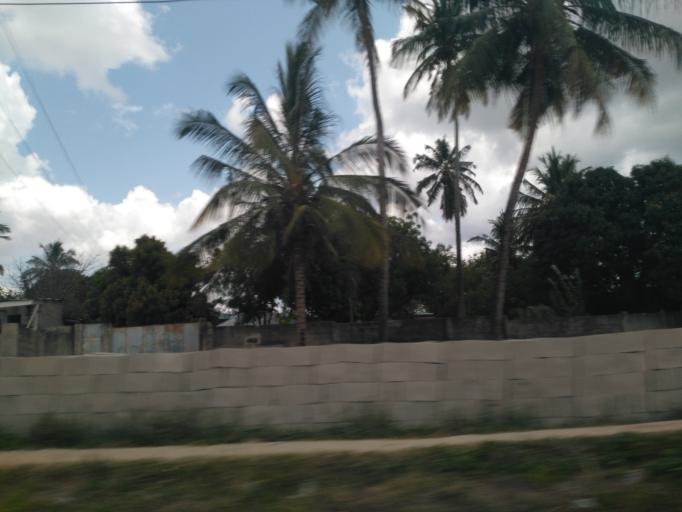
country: TZ
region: Dar es Salaam
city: Dar es Salaam
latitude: -6.8691
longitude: 39.3485
